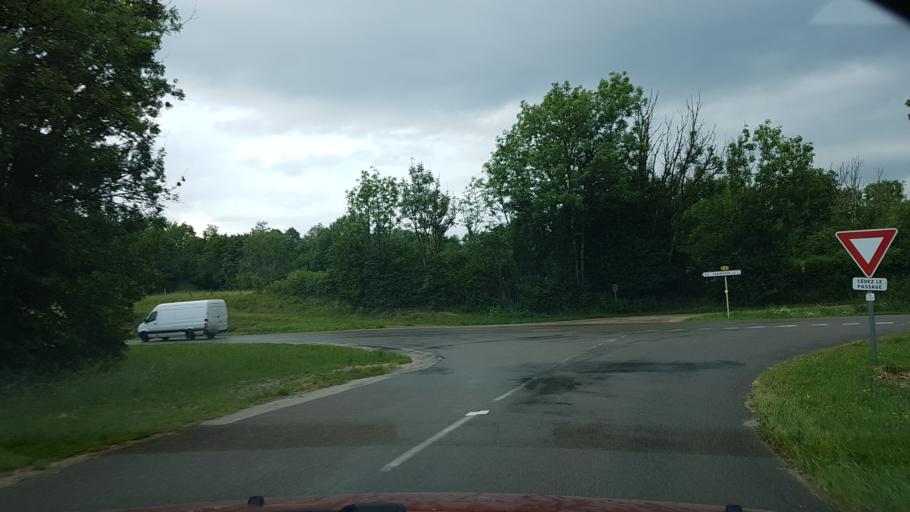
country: FR
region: Franche-Comte
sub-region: Departement du Jura
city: Clairvaux-les-Lacs
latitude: 46.5462
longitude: 5.7477
